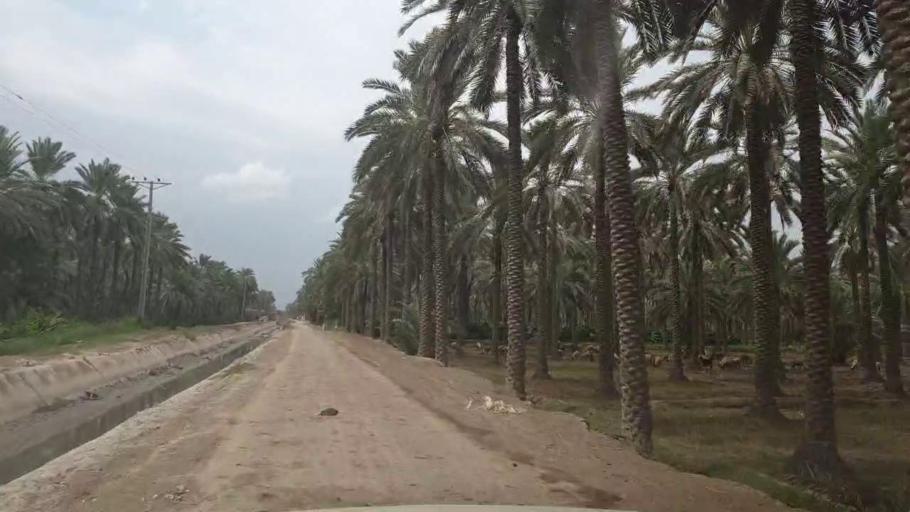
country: PK
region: Sindh
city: Khairpur
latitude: 27.6128
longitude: 68.8046
